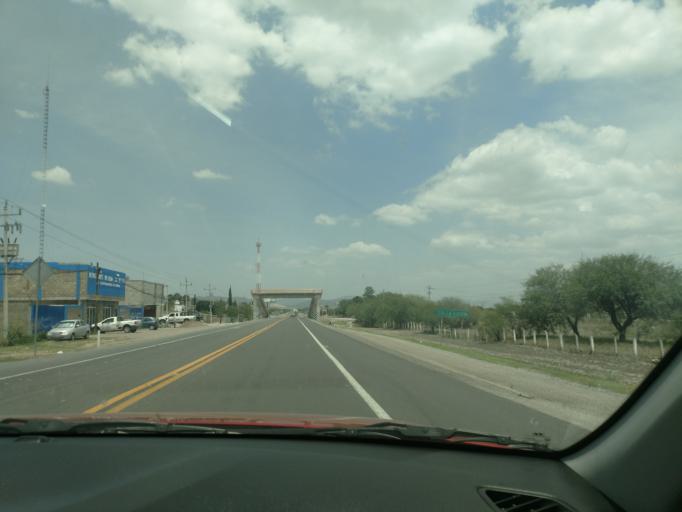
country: MX
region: San Luis Potosi
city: Rio Verde
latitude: 21.9190
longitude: -99.9535
